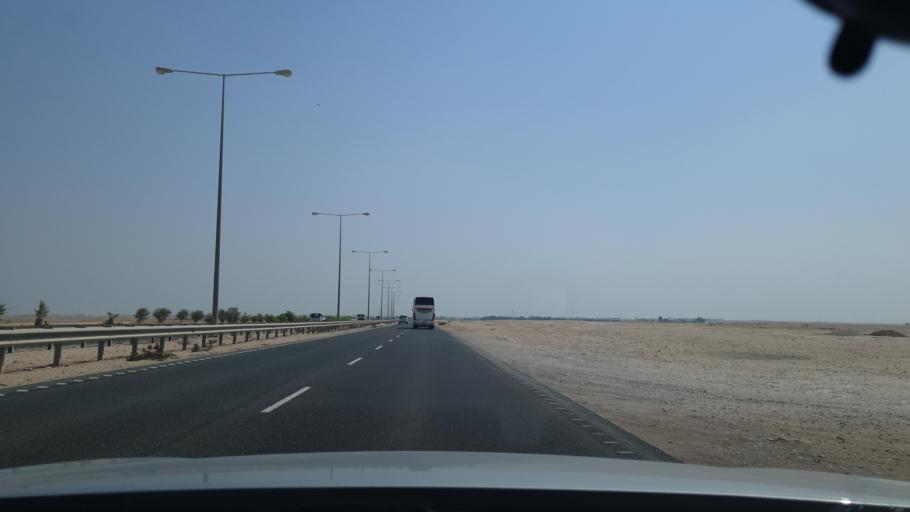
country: QA
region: Al Khawr
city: Al Khawr
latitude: 25.7445
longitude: 51.4829
